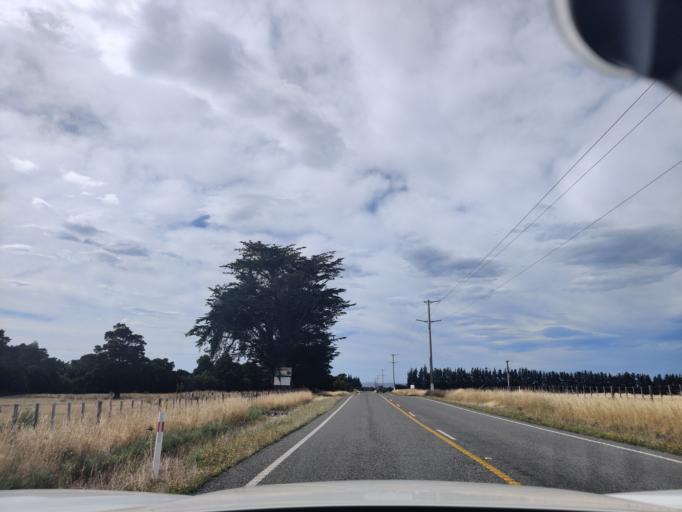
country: NZ
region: Wellington
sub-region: Masterton District
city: Masterton
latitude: -40.8357
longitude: 175.6291
